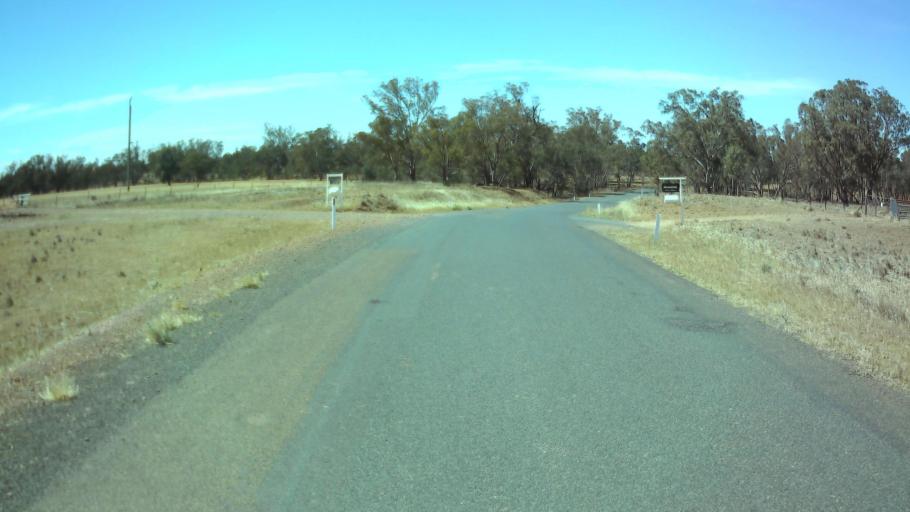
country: AU
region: New South Wales
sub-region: Weddin
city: Grenfell
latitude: -34.1006
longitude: 147.8871
